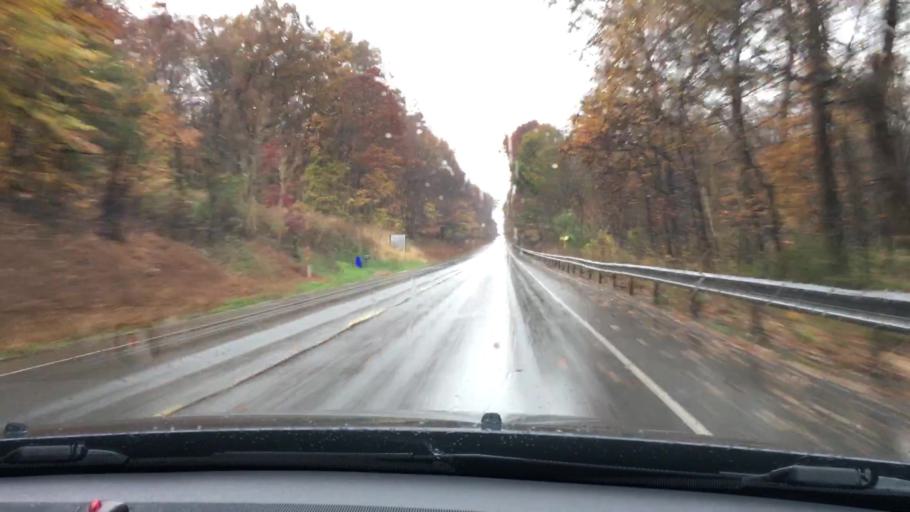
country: US
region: Pennsylvania
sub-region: York County
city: Susquehanna Trails
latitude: 39.8052
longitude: -76.3434
